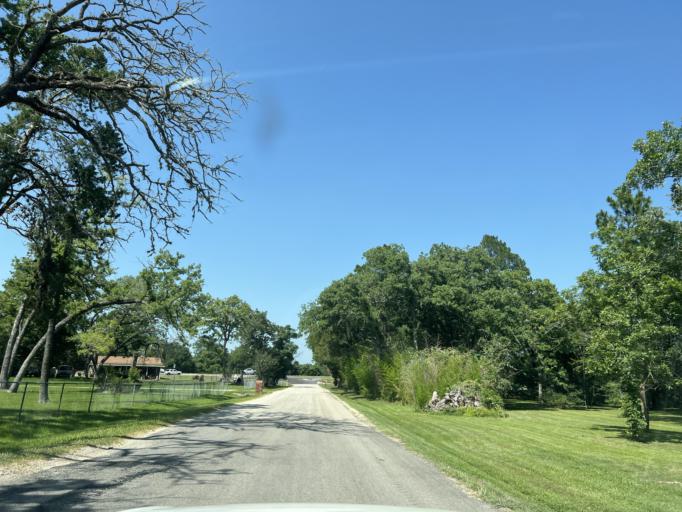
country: US
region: Texas
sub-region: Washington County
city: Brenham
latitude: 30.1818
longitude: -96.4852
